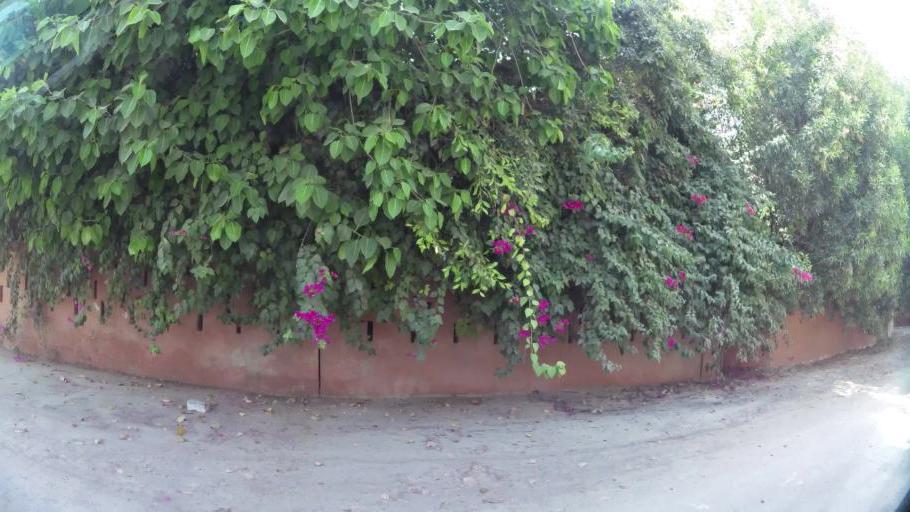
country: AE
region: Ajman
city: Ajman
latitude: 25.3949
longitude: 55.4243
